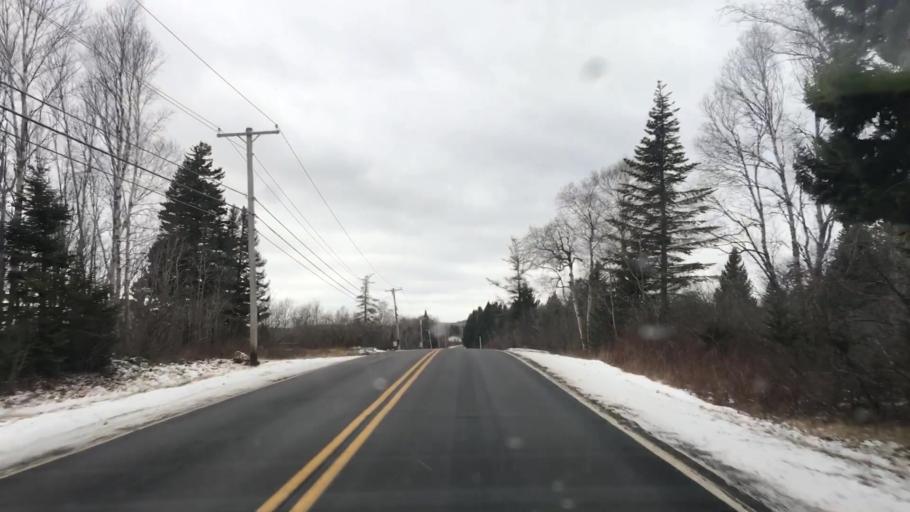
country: US
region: Maine
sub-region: Washington County
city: Machiasport
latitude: 44.7030
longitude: -67.3358
